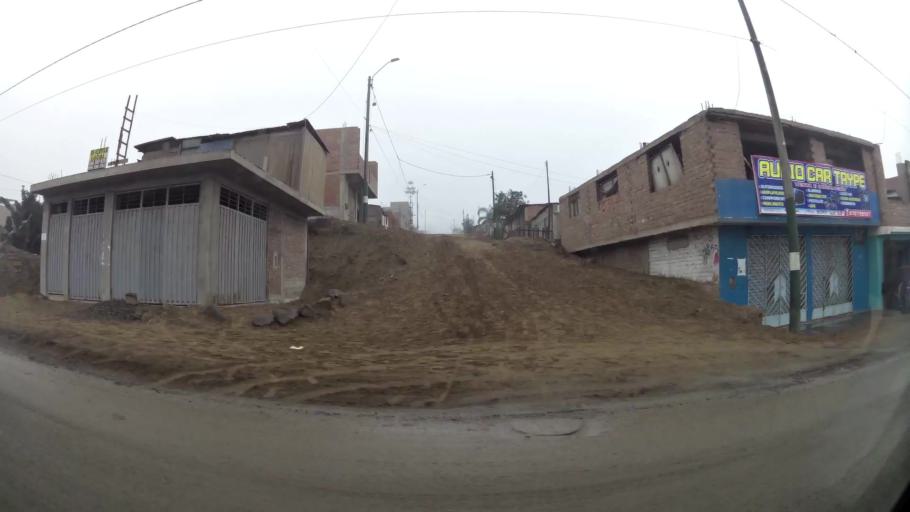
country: PE
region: Lima
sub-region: Lima
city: Santa Rosa
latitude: -11.8312
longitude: -77.1492
